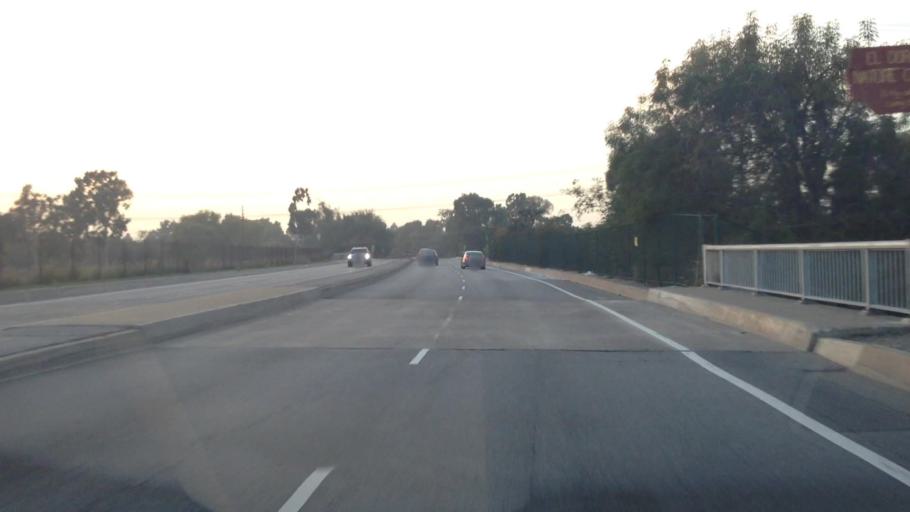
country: US
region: California
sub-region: Orange County
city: Los Alamitos
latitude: 33.8041
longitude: -118.0888
